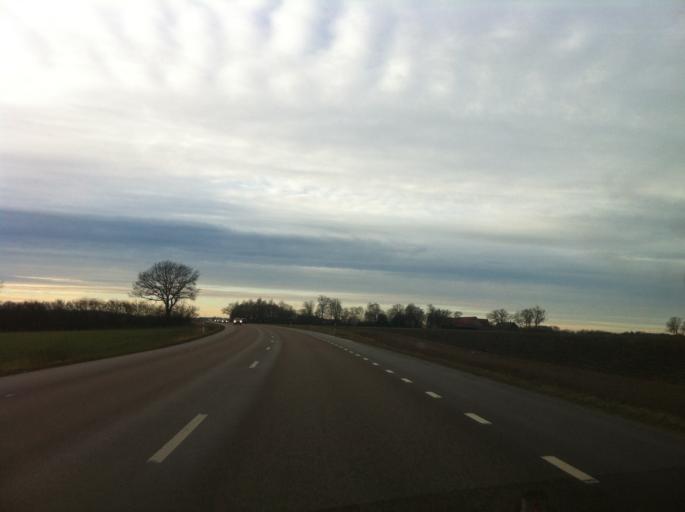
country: SE
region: Skane
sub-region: Helsingborg
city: Hyllinge
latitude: 56.1011
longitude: 12.8254
